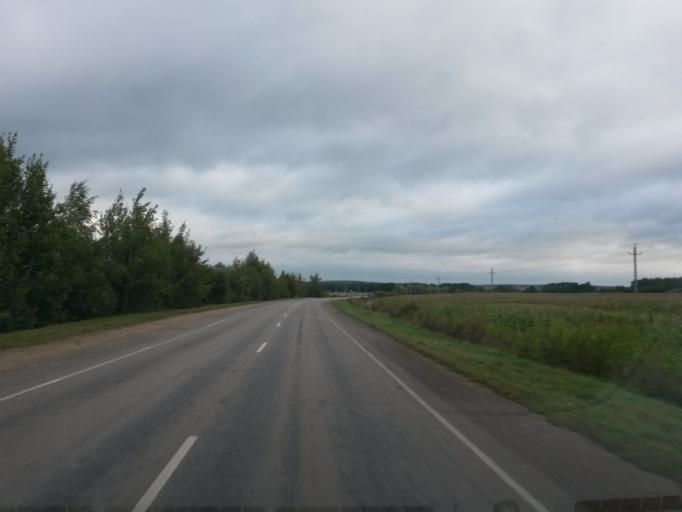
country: RU
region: Moskovskaya
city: Barybino
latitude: 55.2141
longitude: 37.7864
